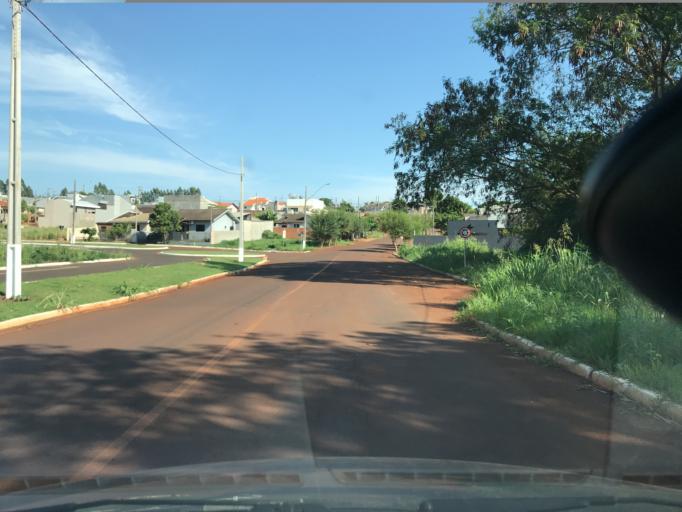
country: BR
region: Parana
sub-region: Palotina
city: Palotina
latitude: -24.2872
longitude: -53.8284
